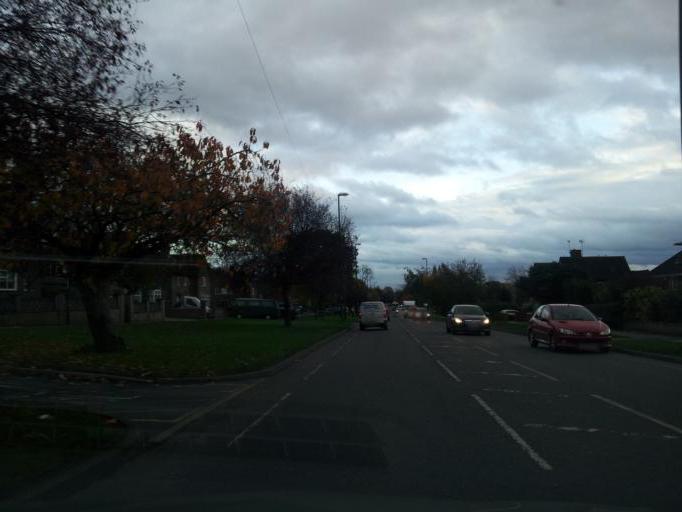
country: GB
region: England
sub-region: Nottinghamshire
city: Kimberley
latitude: 52.9478
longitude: -1.2276
